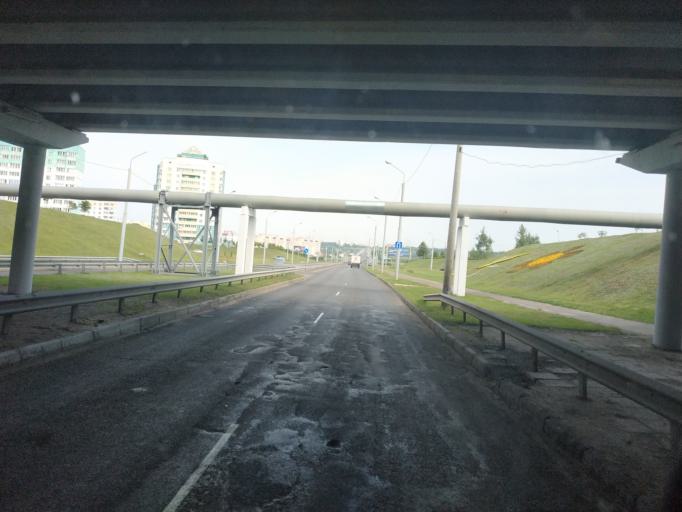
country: BY
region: Mogilev
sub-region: Mahilyowski Rayon
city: Veyno
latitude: 53.8782
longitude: 30.3843
